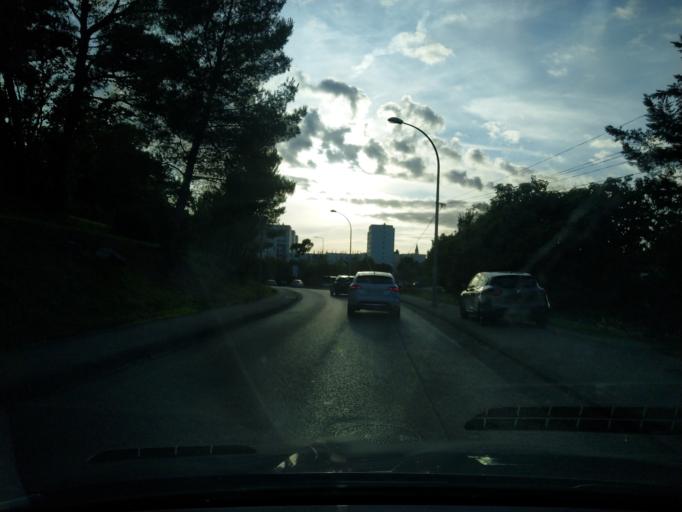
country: FR
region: Provence-Alpes-Cote d'Azur
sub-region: Departement des Bouches-du-Rhone
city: Marseille 11
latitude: 43.2987
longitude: 5.4514
